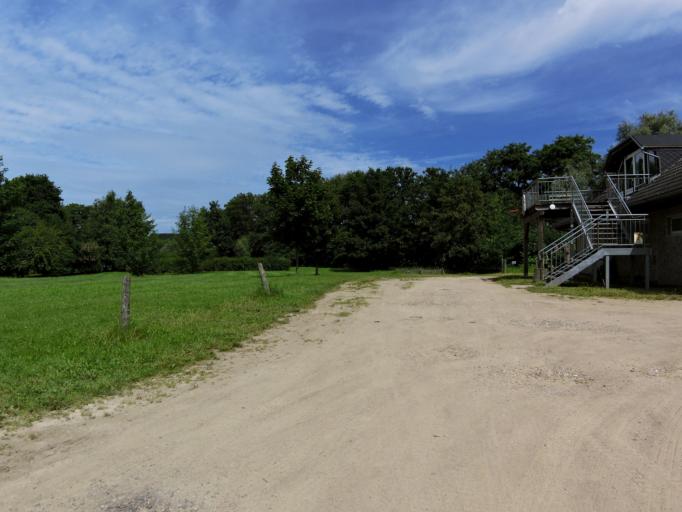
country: DE
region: Mecklenburg-Vorpommern
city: Loitz
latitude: 53.3425
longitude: 13.4453
